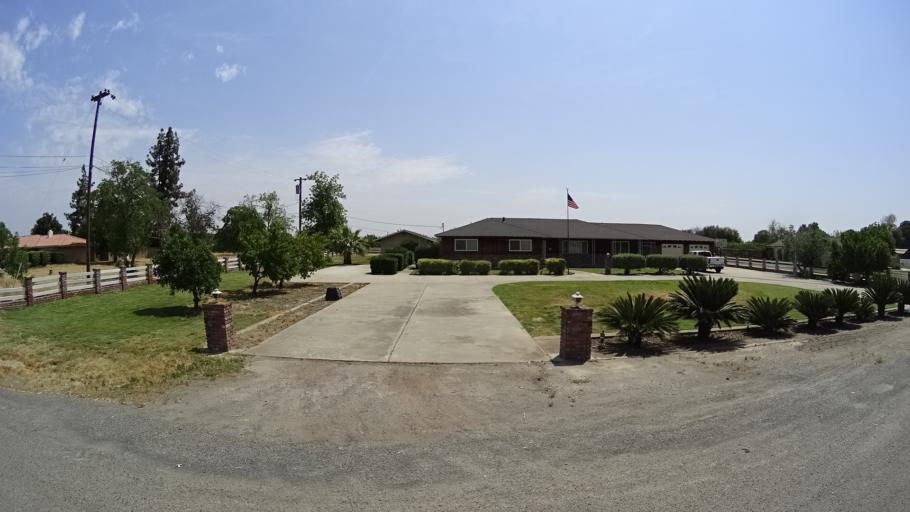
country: US
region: California
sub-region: Kings County
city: Lemoore
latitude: 36.3152
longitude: -119.7627
